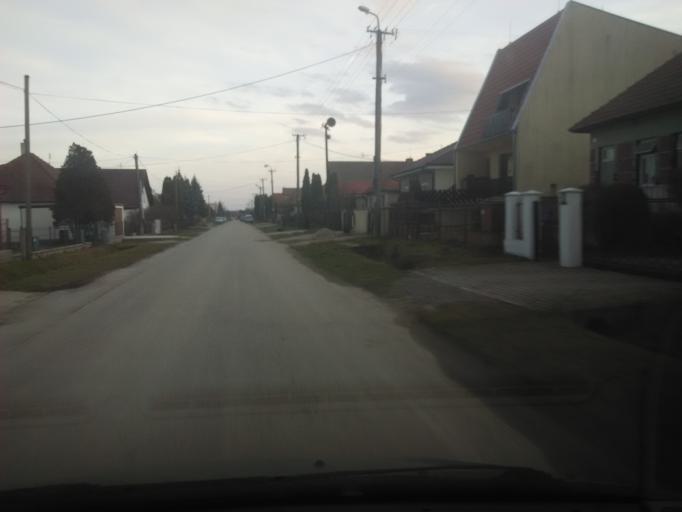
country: SK
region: Nitriansky
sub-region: Okres Nitra
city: Nitra
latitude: 48.3855
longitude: 18.2160
